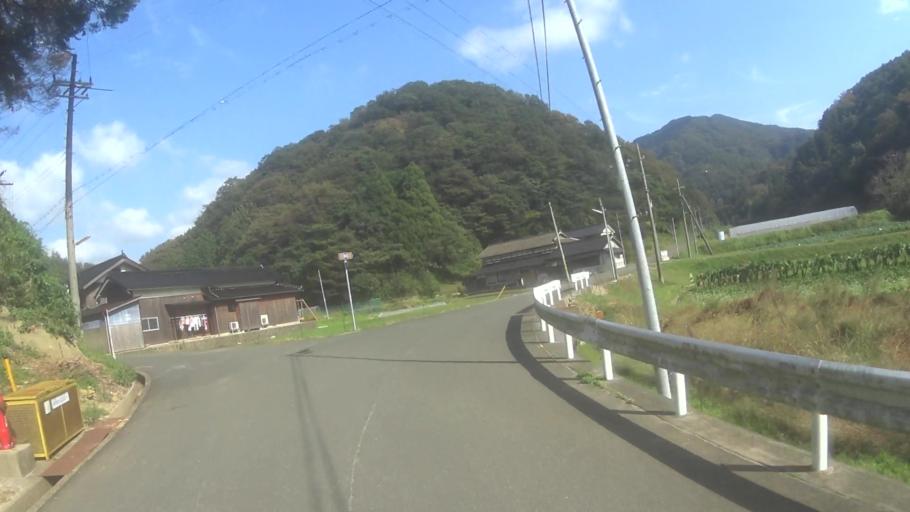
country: JP
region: Kyoto
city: Miyazu
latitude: 35.7164
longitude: 135.1221
